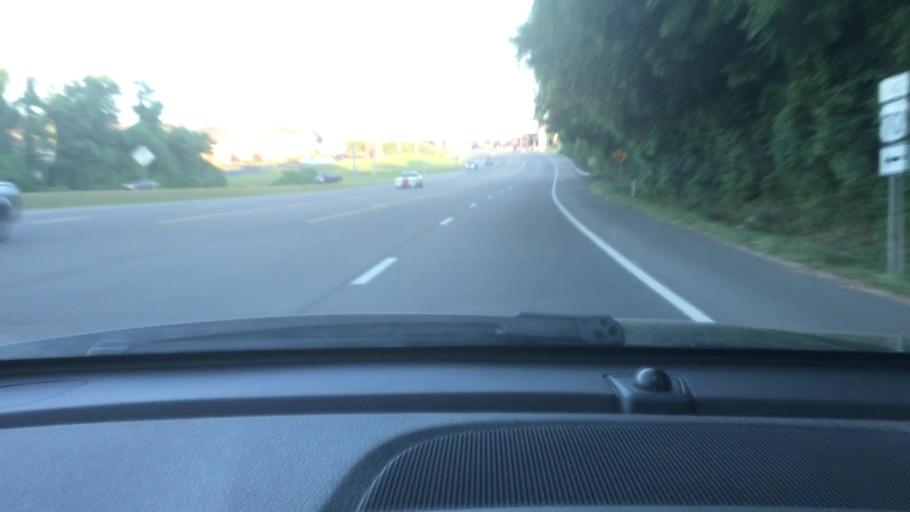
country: US
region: Tennessee
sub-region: Dickson County
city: Dickson
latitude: 36.0819
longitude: -87.3799
